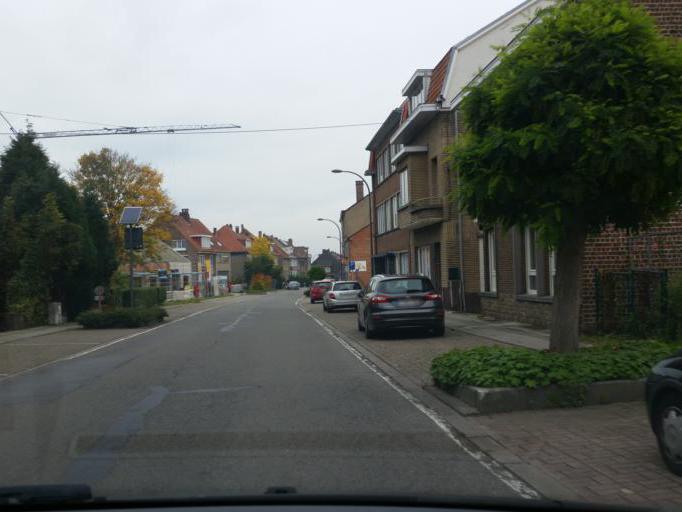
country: BE
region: Flanders
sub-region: Provincie Vlaams-Brabant
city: Drogenbos
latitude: 50.7908
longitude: 4.3147
